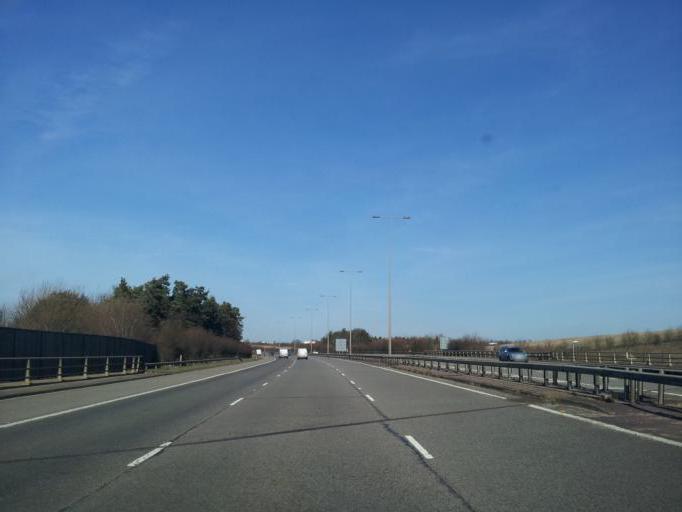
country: GB
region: England
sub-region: Cambridgeshire
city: Great Stukeley
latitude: 52.3695
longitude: -0.2534
